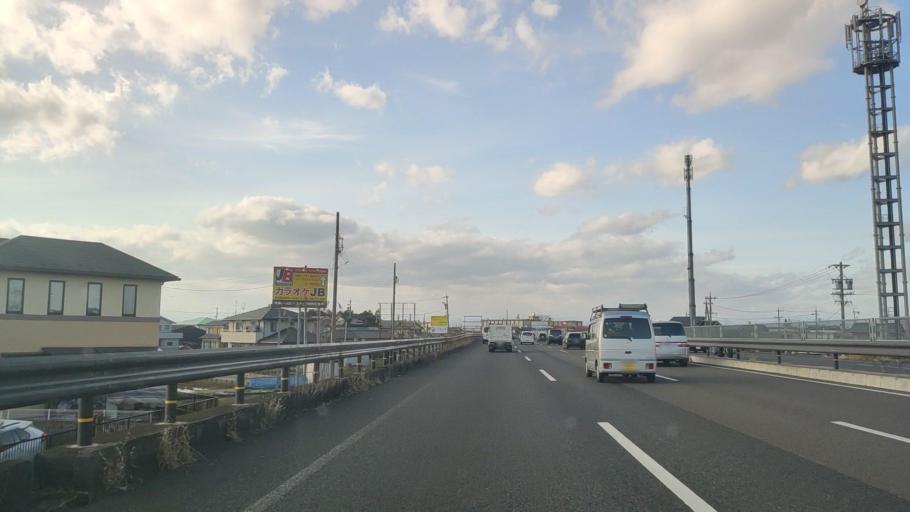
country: JP
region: Aichi
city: Kuroda
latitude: 35.3579
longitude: 136.7850
